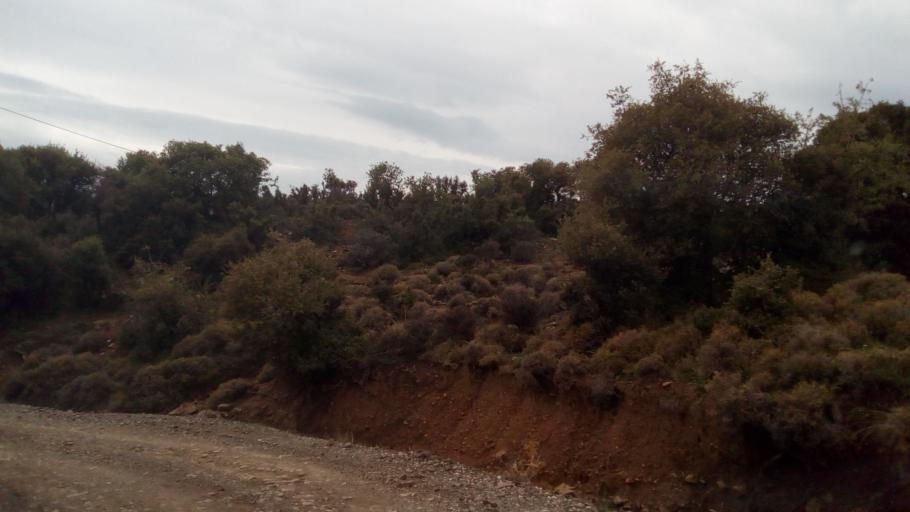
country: GR
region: West Greece
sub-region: Nomos Achaias
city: Selianitika
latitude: 38.4081
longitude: 22.0900
